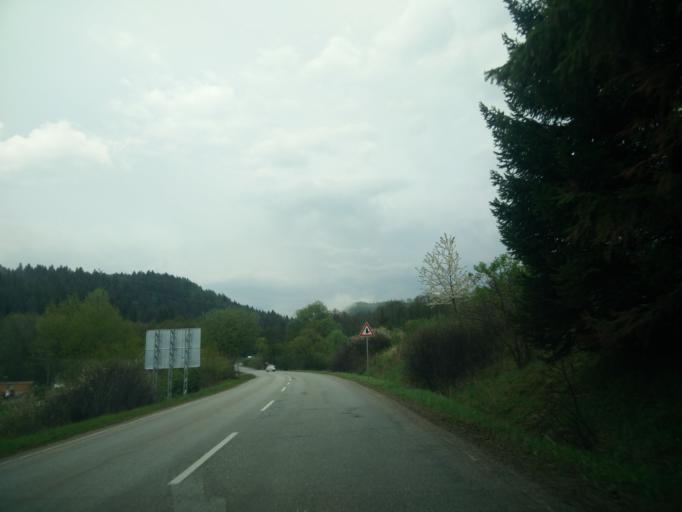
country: SK
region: Banskobystricky
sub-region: Okres Ziar nad Hronom
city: Kremnica
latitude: 48.8380
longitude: 18.8766
